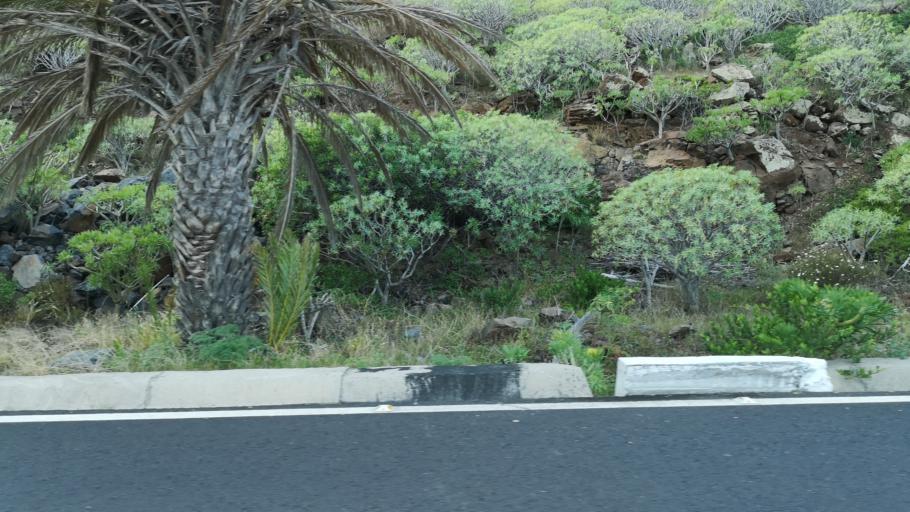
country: ES
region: Canary Islands
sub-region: Provincia de Santa Cruz de Tenerife
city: San Sebastian de la Gomera
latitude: 28.0836
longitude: -17.1332
